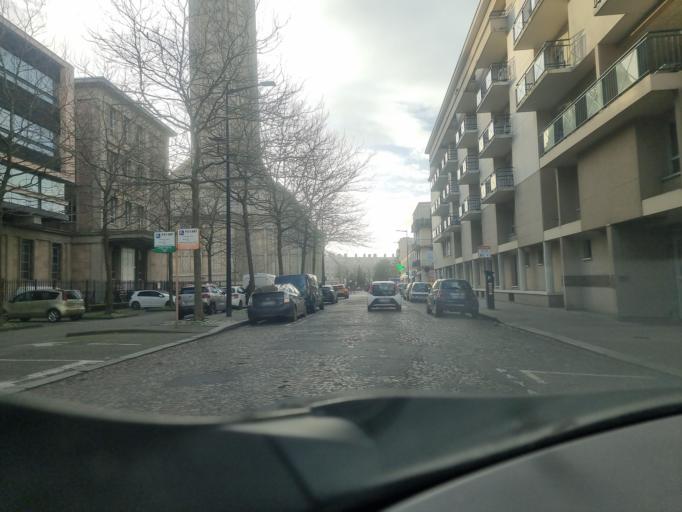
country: FR
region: Haute-Normandie
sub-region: Departement de la Seine-Maritime
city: Le Havre
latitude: 49.4912
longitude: 0.1027
